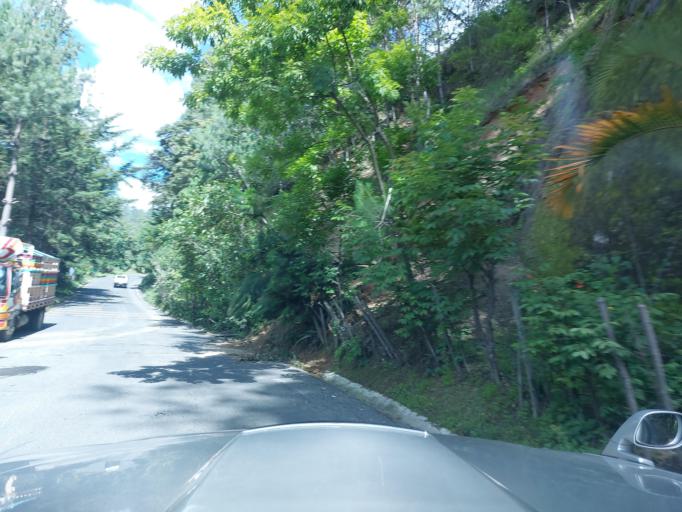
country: GT
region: Chimaltenango
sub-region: Municipio de Santa Cruz Balanya
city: Santa Cruz Balanya
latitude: 14.6965
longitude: -90.8953
